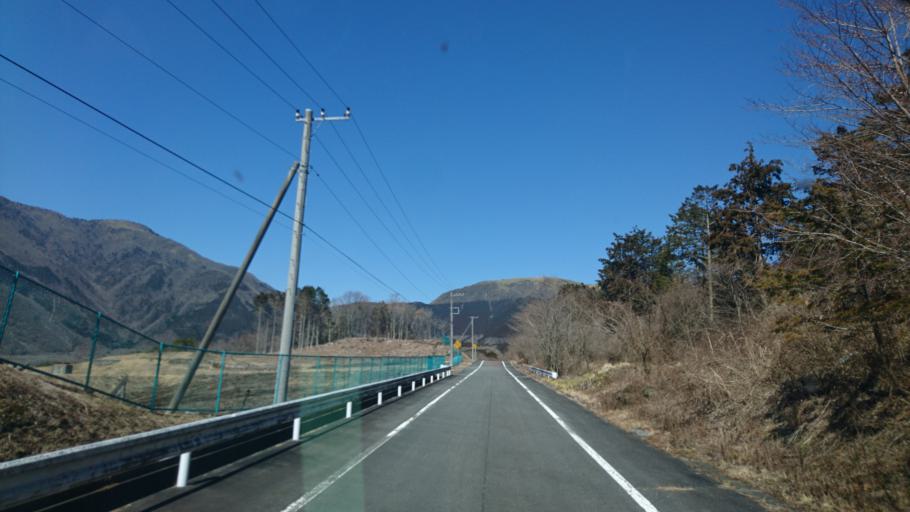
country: JP
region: Yamanashi
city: Fujikawaguchiko
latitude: 35.4153
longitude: 138.5973
